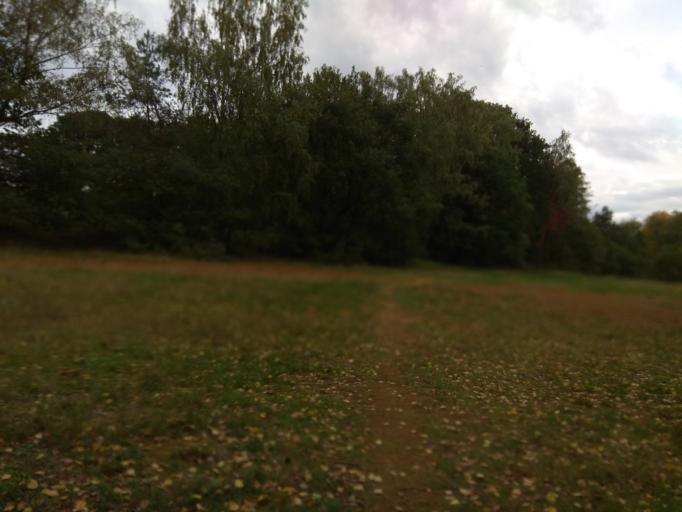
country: DE
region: North Rhine-Westphalia
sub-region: Regierungsbezirk Munster
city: Klein Reken
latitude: 51.7399
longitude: 7.0418
